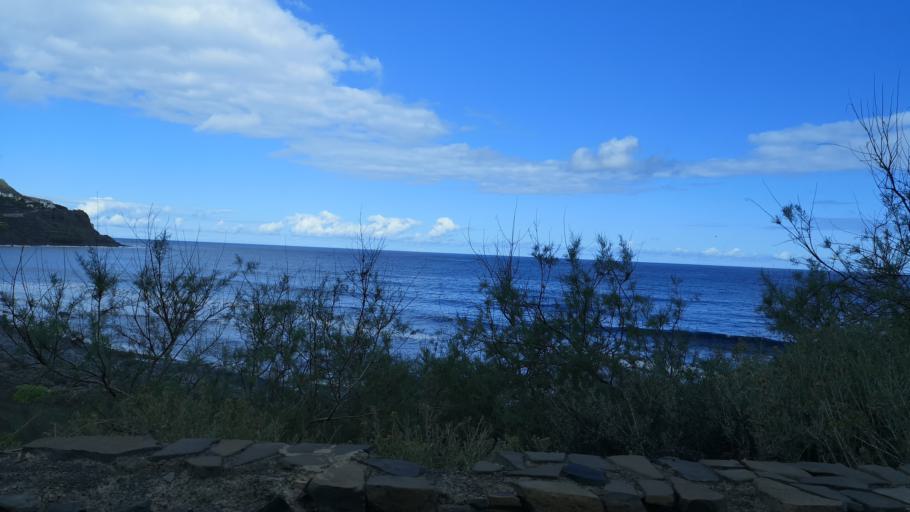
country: ES
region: Canary Islands
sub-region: Provincia de Santa Cruz de Tenerife
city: Hermigua
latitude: 28.1771
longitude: -17.1777
